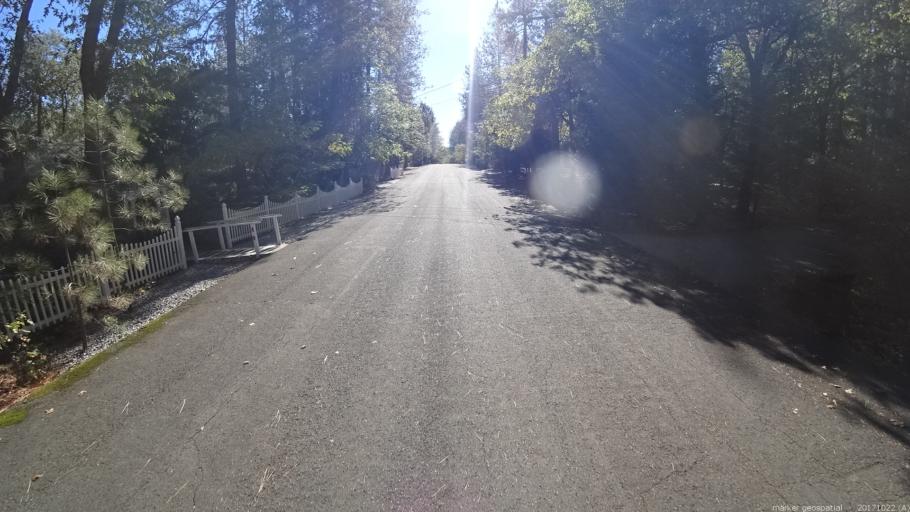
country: US
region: California
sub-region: Shasta County
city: Central Valley (historical)
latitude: 40.8878
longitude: -122.3865
